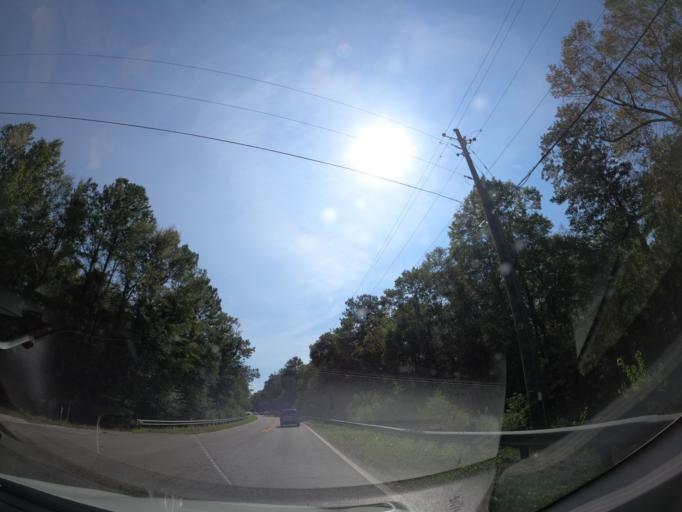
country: US
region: Florida
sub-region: Okaloosa County
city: Crestview
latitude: 30.7497
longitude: -86.6209
